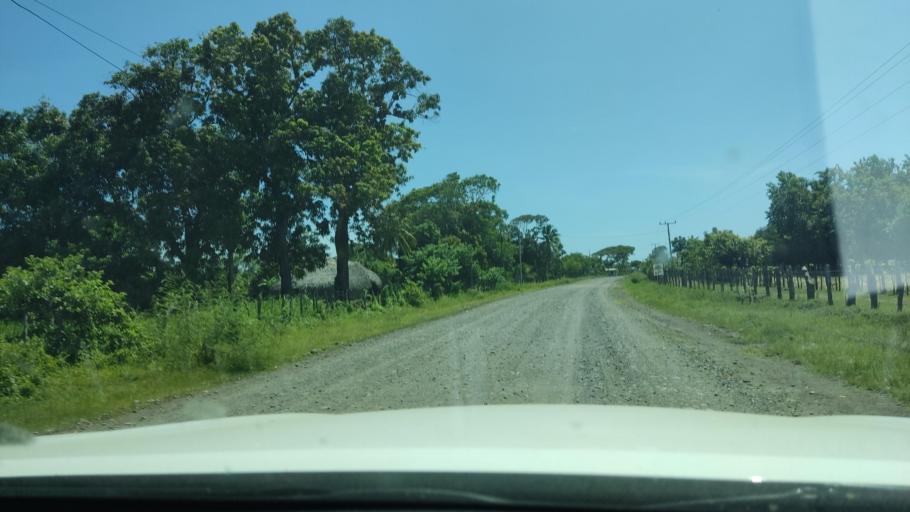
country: SV
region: Ahuachapan
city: San Francisco Menendez
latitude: 13.7649
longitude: -90.1635
